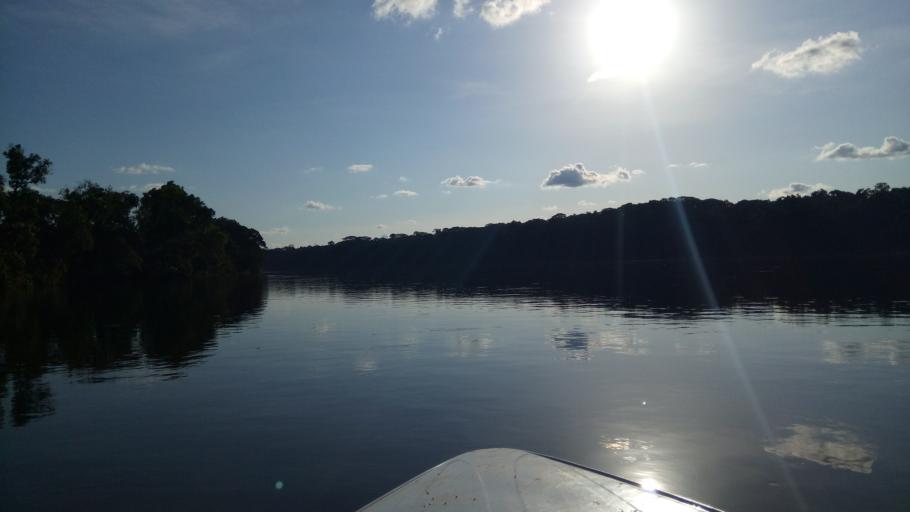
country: CD
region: Eastern Province
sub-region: Sous-Region de la Tshopo
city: Yangambi
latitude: 0.2554
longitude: 24.0560
